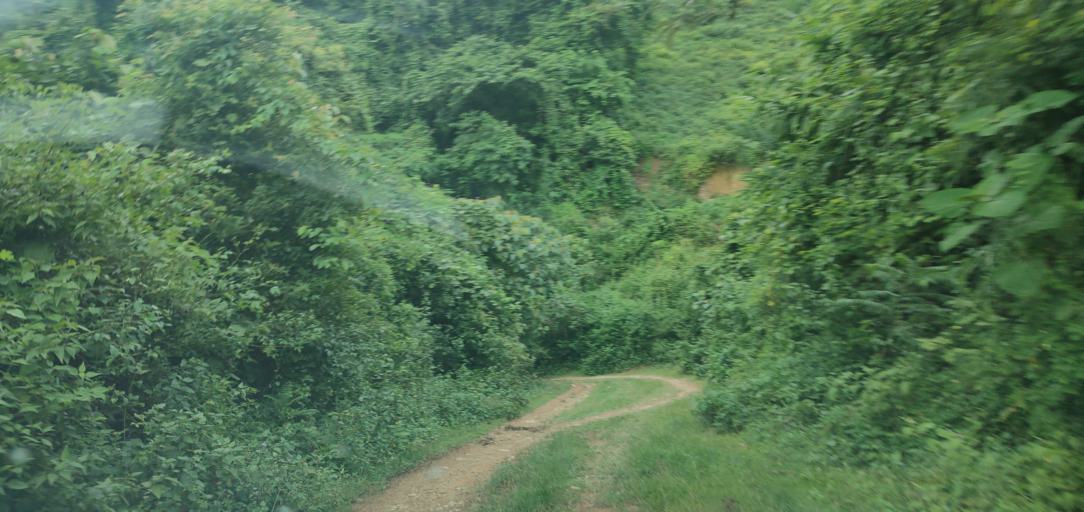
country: LA
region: Phongsali
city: Phongsali
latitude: 21.4398
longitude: 102.3287
